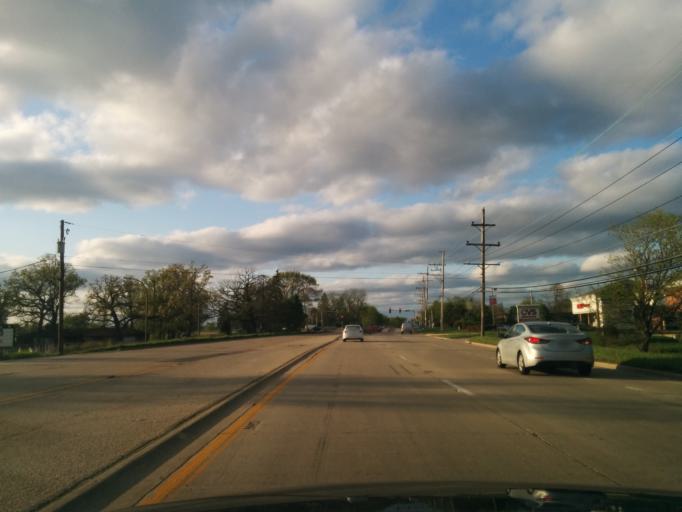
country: US
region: Illinois
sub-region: DuPage County
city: Wayne
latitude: 41.9448
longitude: -88.2083
